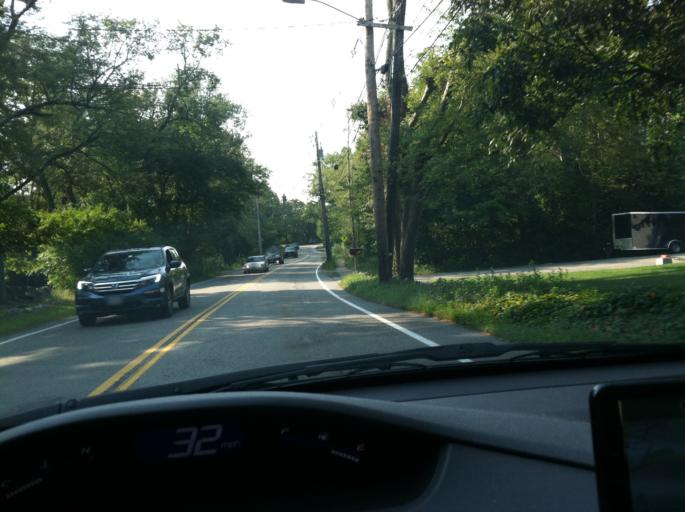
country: US
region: Massachusetts
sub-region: Middlesex County
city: Bedford
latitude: 42.5007
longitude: -71.2508
